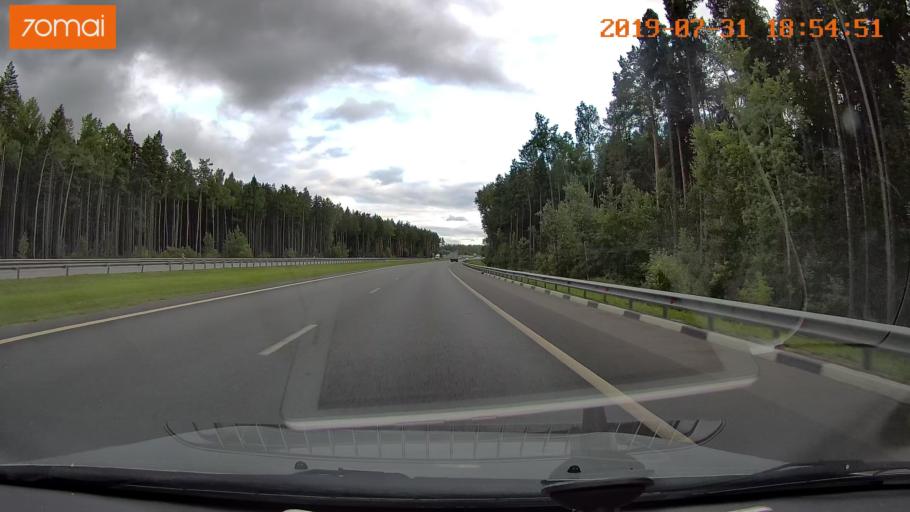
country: RU
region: Moskovskaya
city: Raduzhnyy
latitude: 55.1836
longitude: 38.6695
